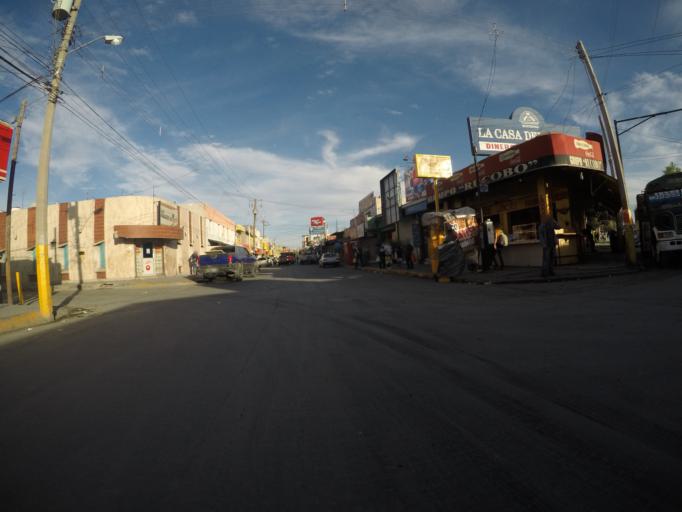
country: MX
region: Chihuahua
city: Ciudad Juarez
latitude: 31.7361
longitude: -106.4856
